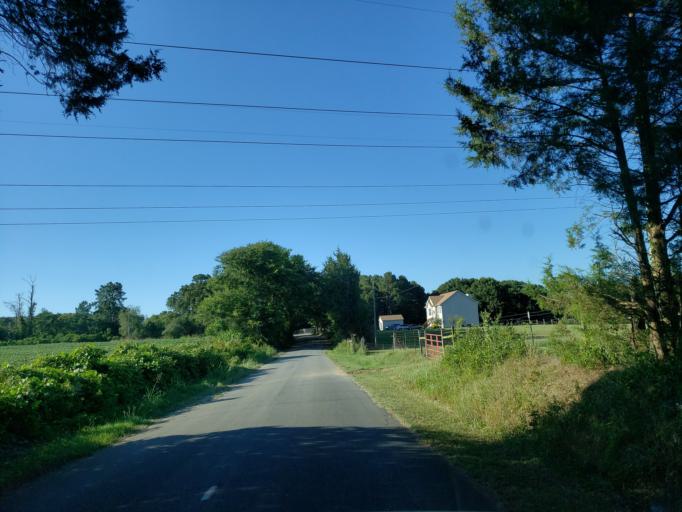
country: US
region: Georgia
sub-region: Bartow County
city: Euharlee
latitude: 34.1170
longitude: -84.9894
